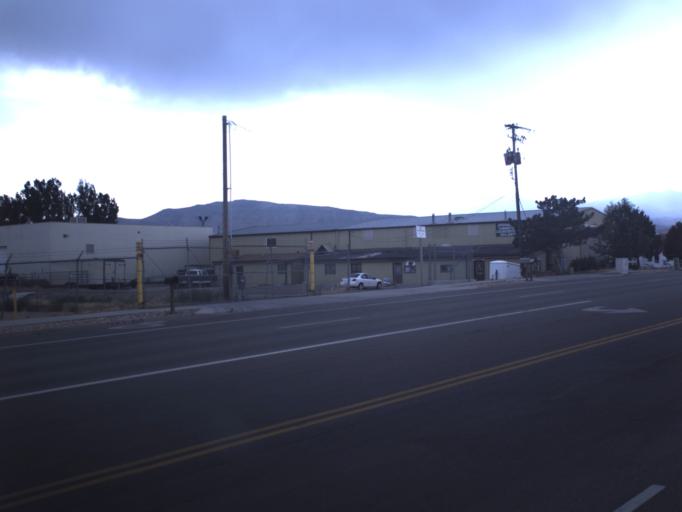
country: US
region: Utah
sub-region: Salt Lake County
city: Riverton
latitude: 40.5224
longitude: -111.9680
